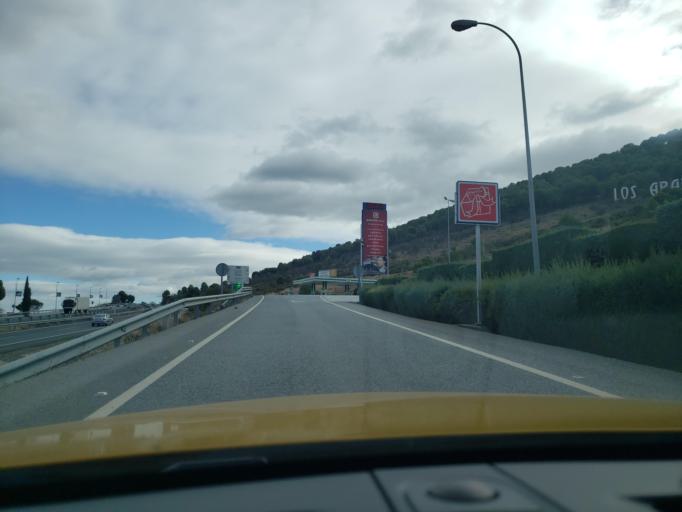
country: ES
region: Andalusia
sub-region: Provincia de Granada
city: Loja
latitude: 37.1650
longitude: -4.1698
